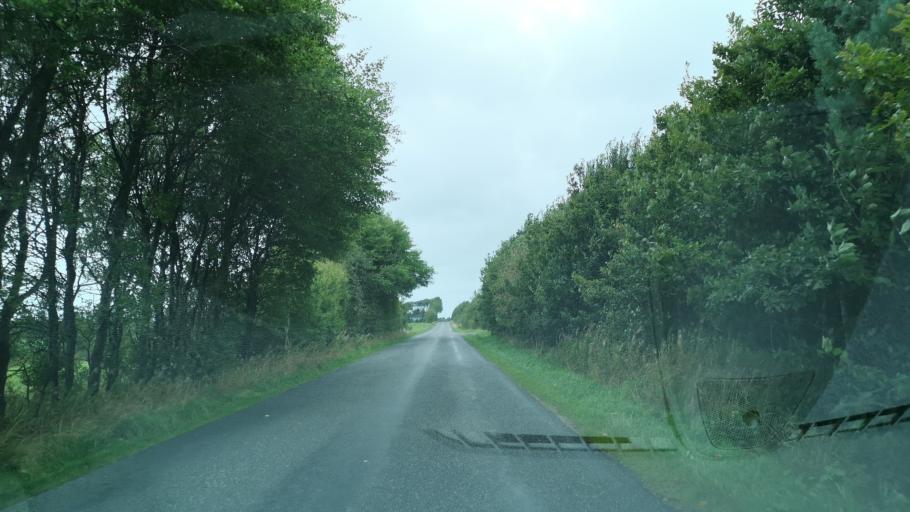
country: DK
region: Central Jutland
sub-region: Ringkobing-Skjern Kommune
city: Videbaek
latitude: 56.0601
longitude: 8.6748
